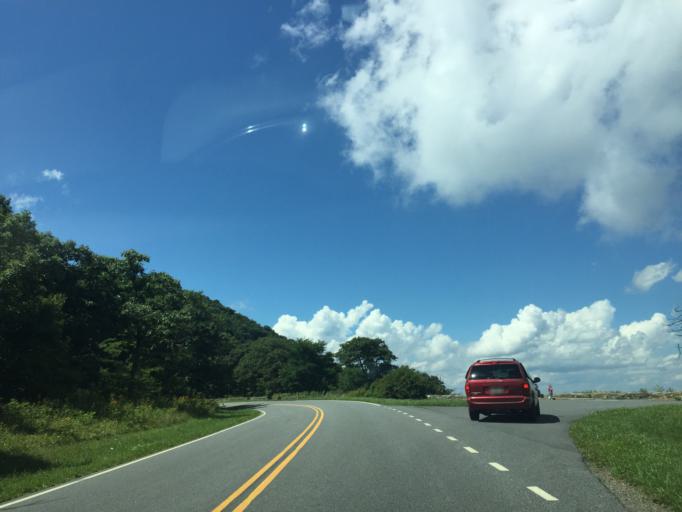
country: US
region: Virginia
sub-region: Rappahannock County
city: Washington
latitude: 38.7583
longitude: -78.2620
